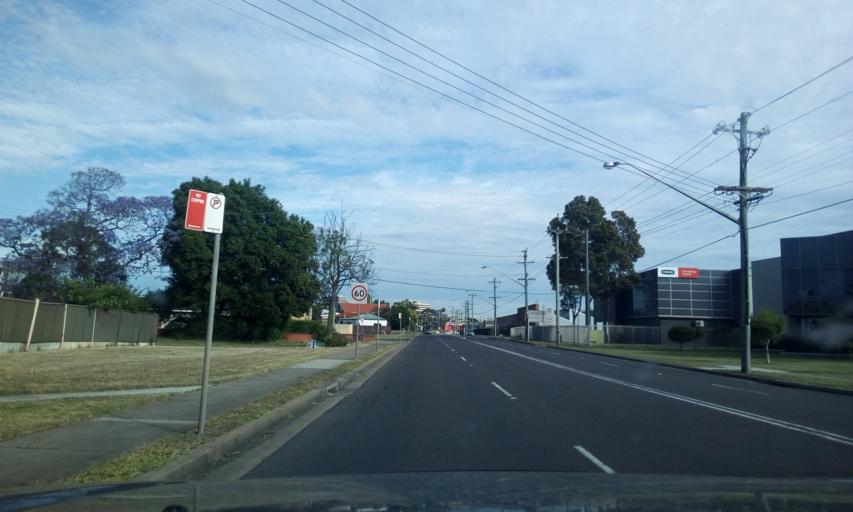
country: AU
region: New South Wales
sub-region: Fairfield
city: Liverpool
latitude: -33.9314
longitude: 150.9331
